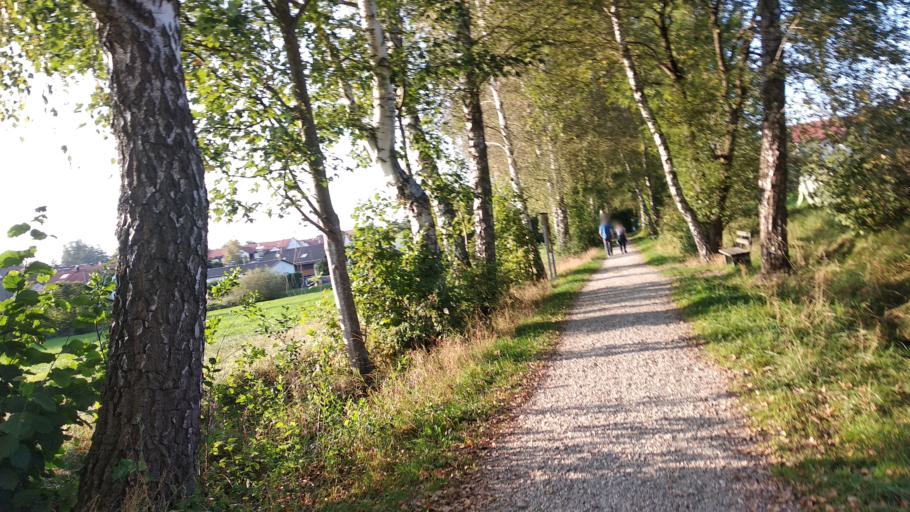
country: DE
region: Bavaria
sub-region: Upper Bavaria
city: Isen
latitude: 48.2080
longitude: 12.0637
